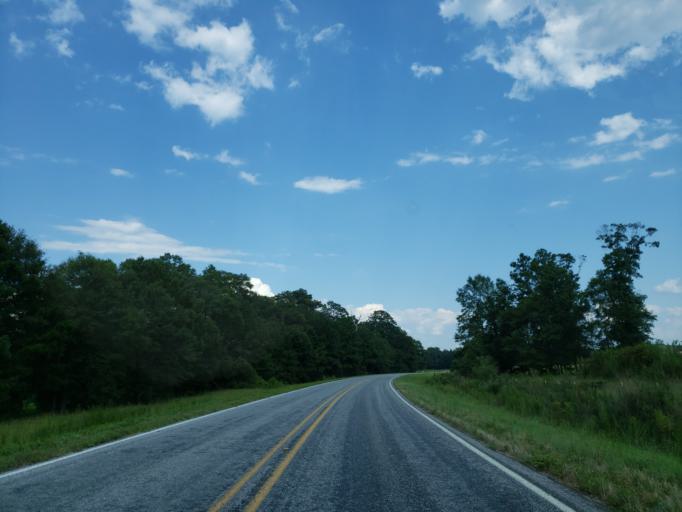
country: US
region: Mississippi
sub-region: Jones County
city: Ellisville
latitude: 31.6234
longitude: -89.3606
